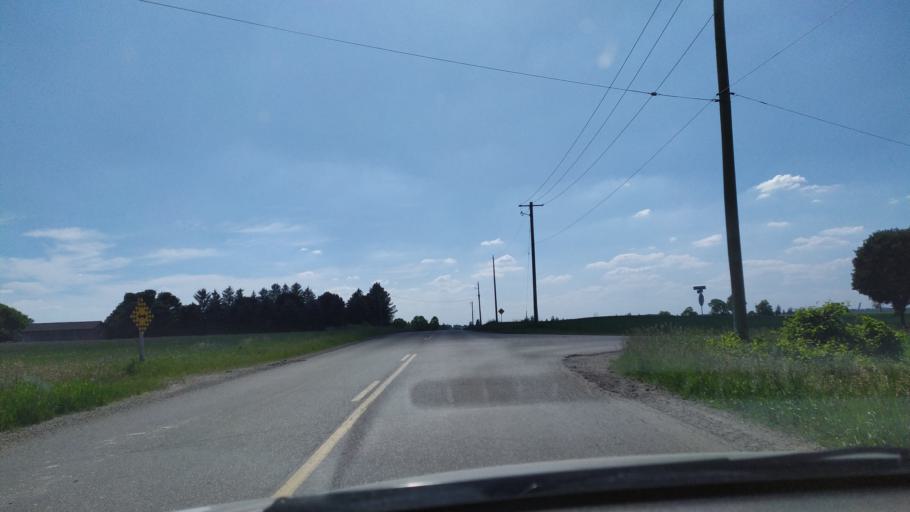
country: CA
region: Ontario
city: Kitchener
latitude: 43.3756
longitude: -80.5287
